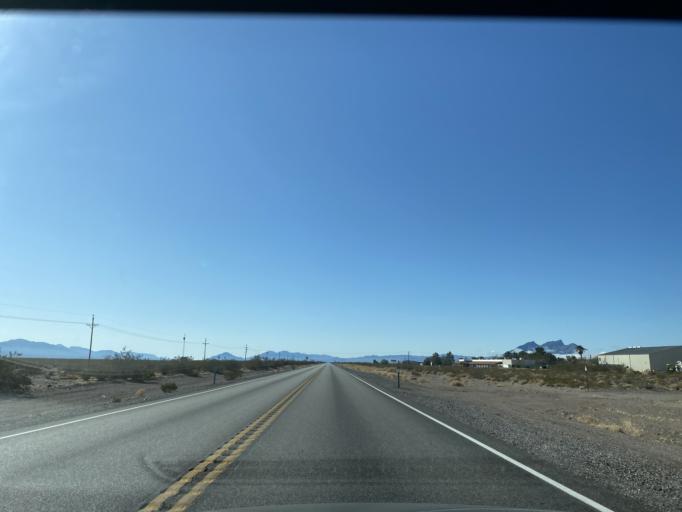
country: US
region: Nevada
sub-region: Nye County
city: Pahrump
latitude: 36.4987
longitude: -116.4214
